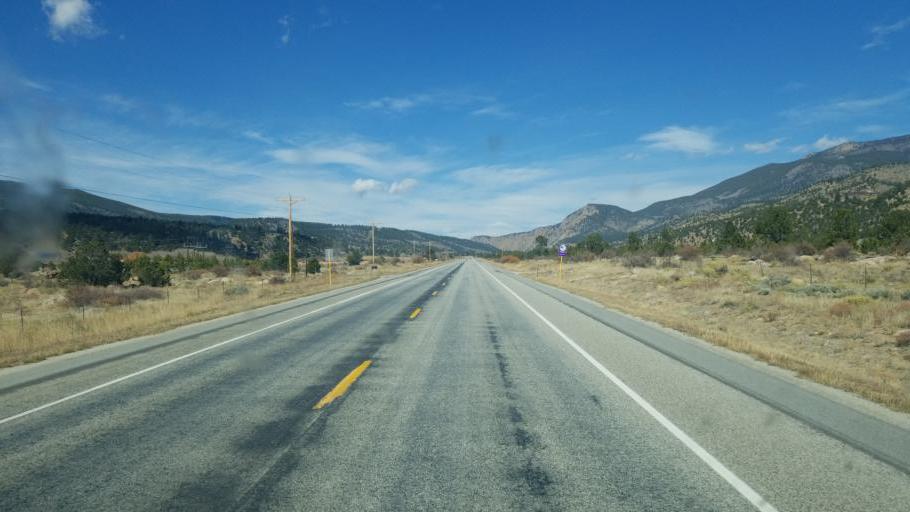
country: US
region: Colorado
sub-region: Chaffee County
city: Buena Vista
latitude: 38.9445
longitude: -106.1927
